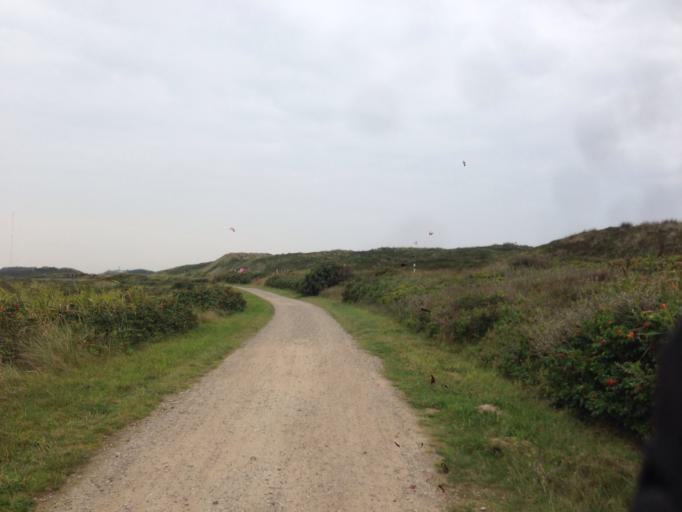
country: DE
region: Schleswig-Holstein
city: Westerland
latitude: 54.8281
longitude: 8.2913
